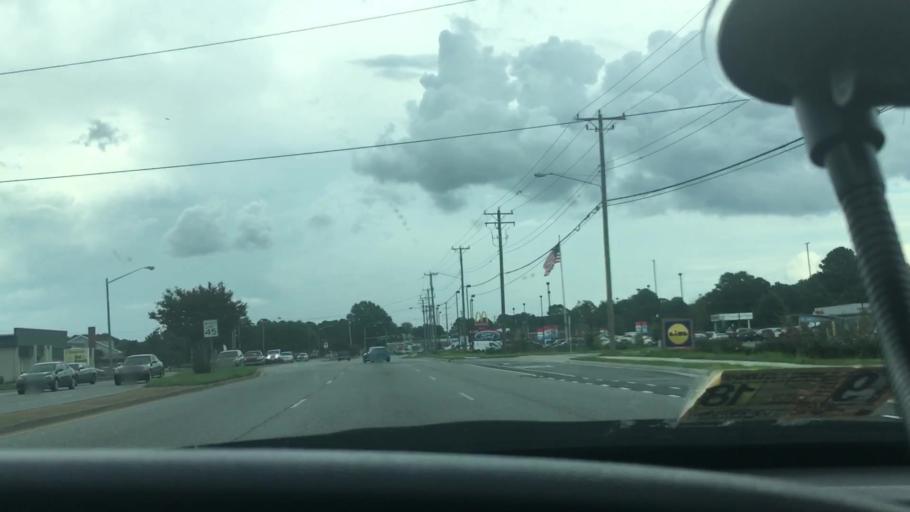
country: US
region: Virginia
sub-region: City of Portsmouth
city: Portsmouth Heights
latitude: 36.8243
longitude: -76.4088
